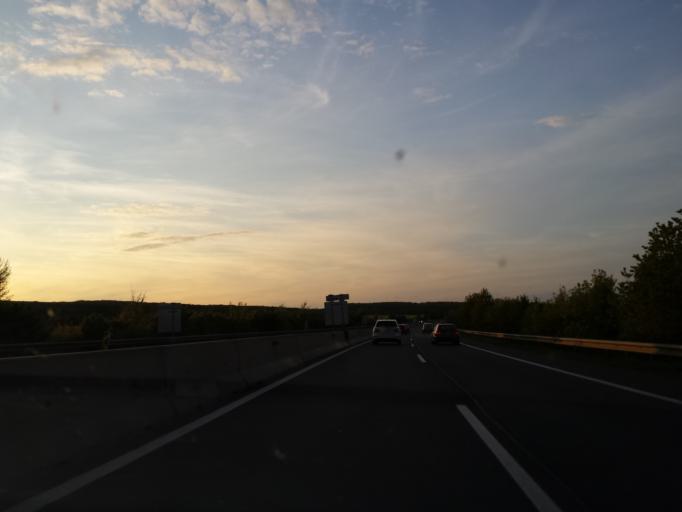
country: AT
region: Burgenland
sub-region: Politischer Bezirk Neusiedl am See
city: Parndorf
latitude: 47.9836
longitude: 16.8369
